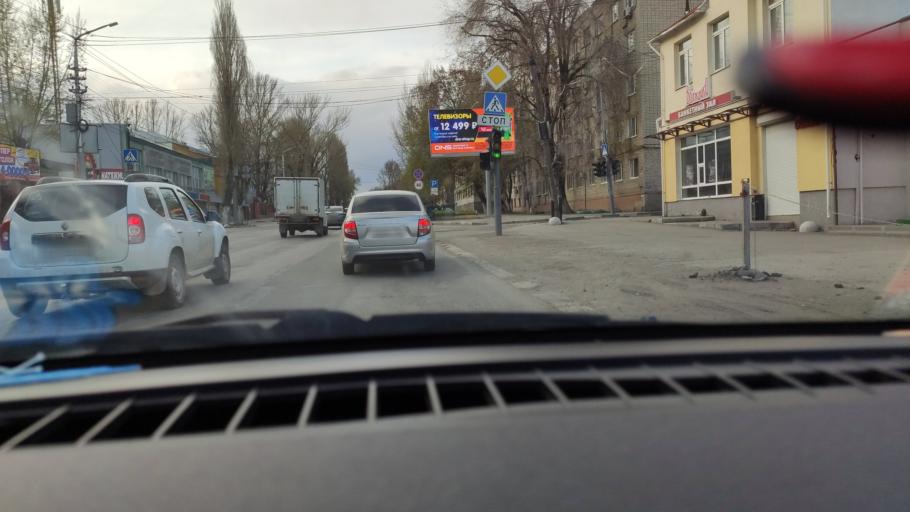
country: RU
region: Saratov
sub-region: Saratovskiy Rayon
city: Saratov
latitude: 51.5536
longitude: 46.0088
